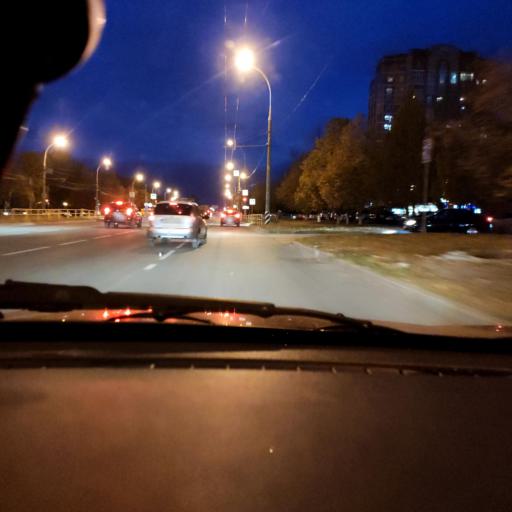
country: RU
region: Samara
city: Tol'yatti
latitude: 53.5123
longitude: 49.2935
